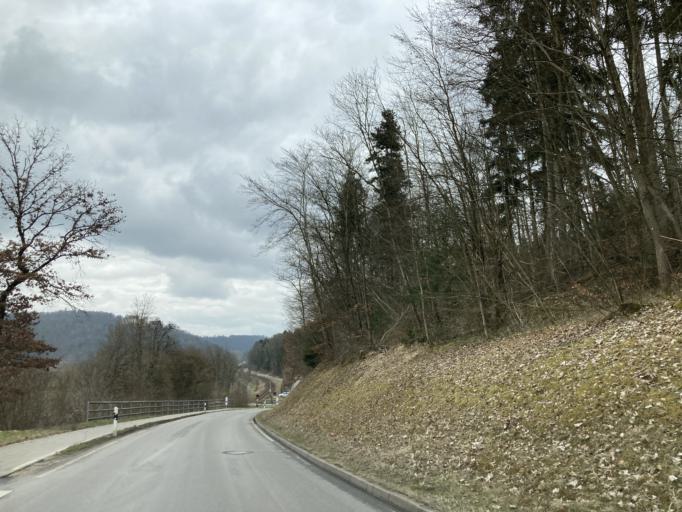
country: DE
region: Baden-Wuerttemberg
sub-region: Tuebingen Region
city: Haigerloch
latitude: 48.4425
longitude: 8.7979
